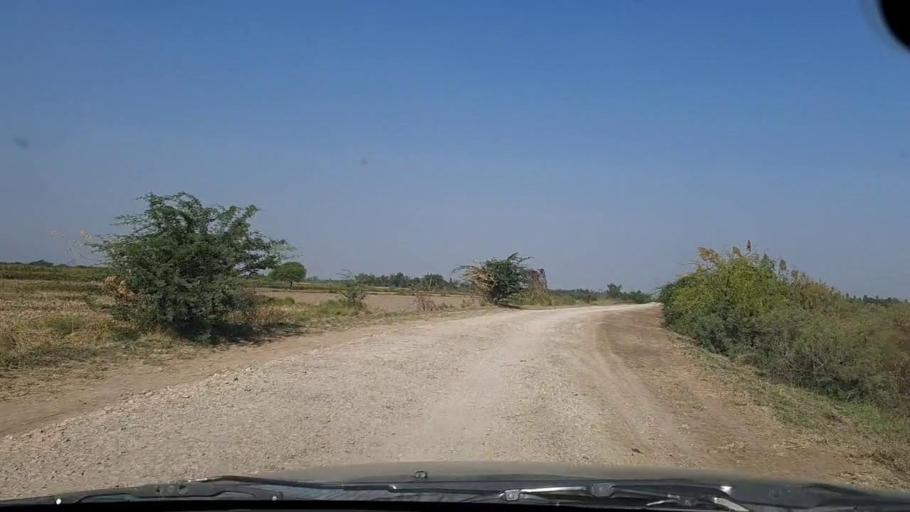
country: PK
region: Sindh
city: Chuhar Jamali
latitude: 24.4375
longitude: 67.7990
